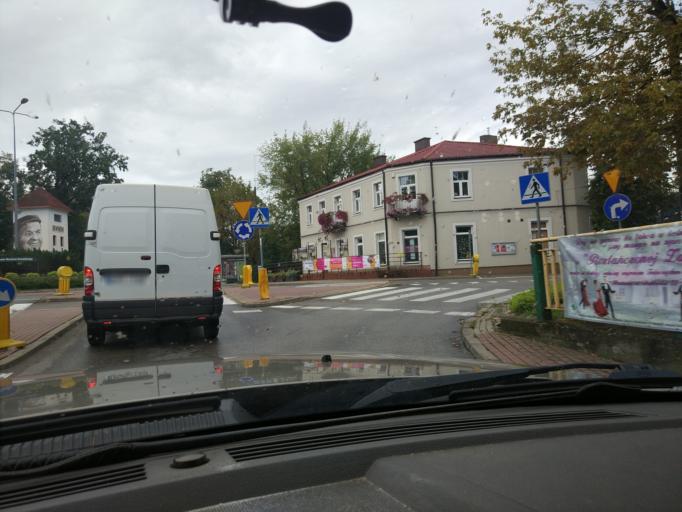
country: PL
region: Masovian Voivodeship
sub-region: Powiat pruszkowski
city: Brwinow
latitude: 52.1407
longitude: 20.7180
